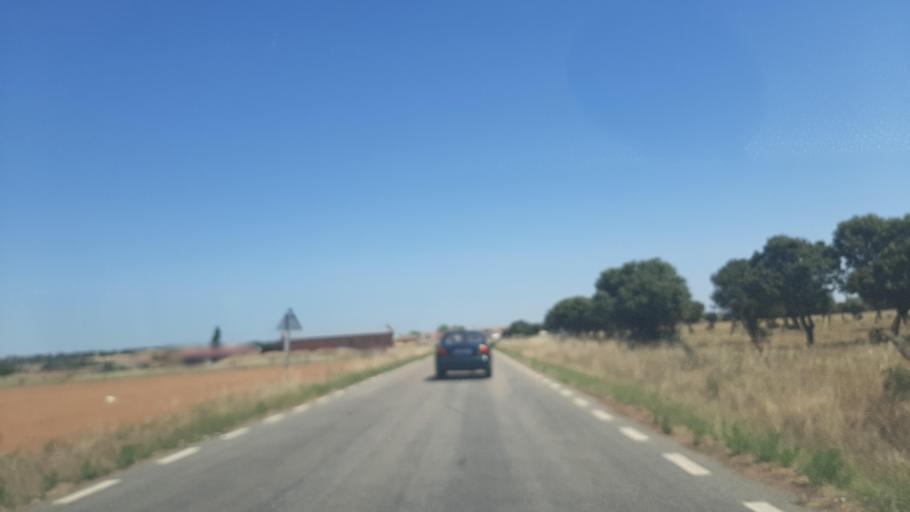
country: ES
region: Castille and Leon
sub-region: Provincia de Salamanca
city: Cabrillas
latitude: 40.7317
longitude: -6.1774
